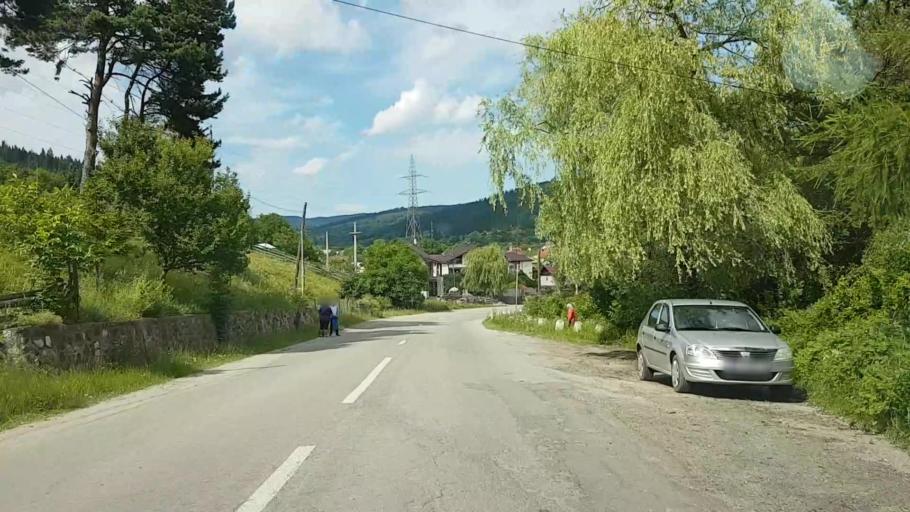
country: RO
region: Neamt
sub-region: Comuna Hangu
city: Hangu
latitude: 47.0592
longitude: 26.0325
